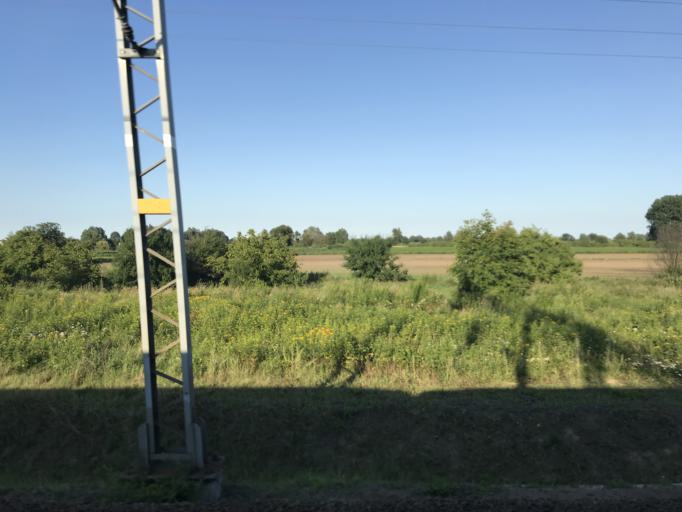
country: PL
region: Pomeranian Voivodeship
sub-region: Powiat gdanski
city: Pruszcz Gdanski
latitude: 54.2733
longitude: 18.6444
